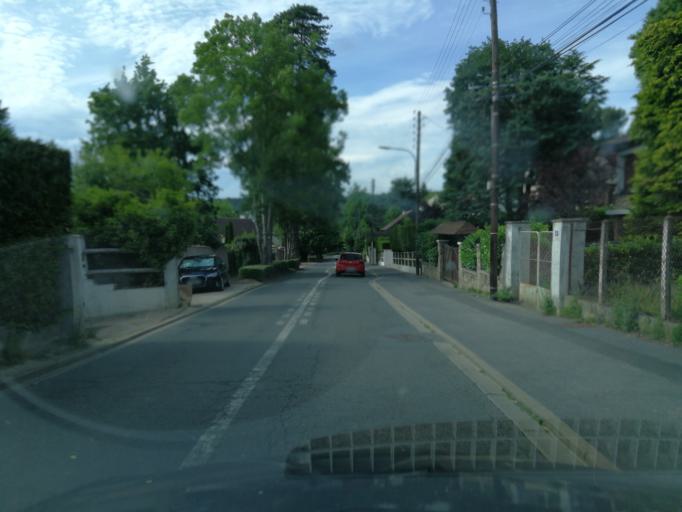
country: FR
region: Ile-de-France
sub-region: Departement de l'Essonne
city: Gif-sur-Yvette
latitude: 48.6952
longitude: 2.1067
